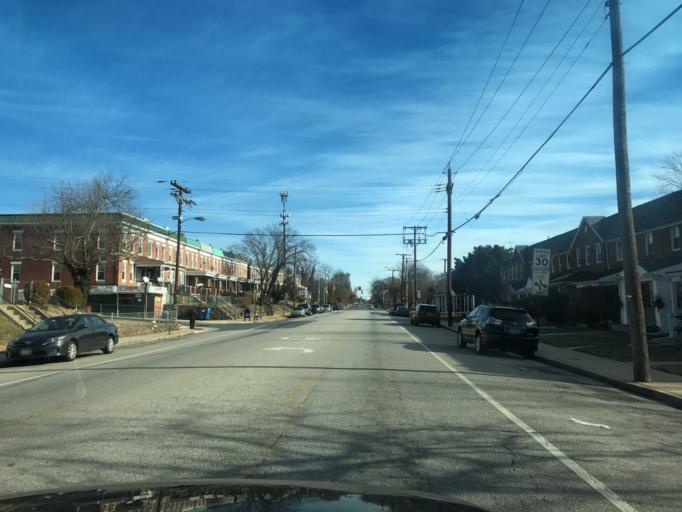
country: US
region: Maryland
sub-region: Baltimore County
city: Charlestown
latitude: 39.2814
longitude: -76.6954
